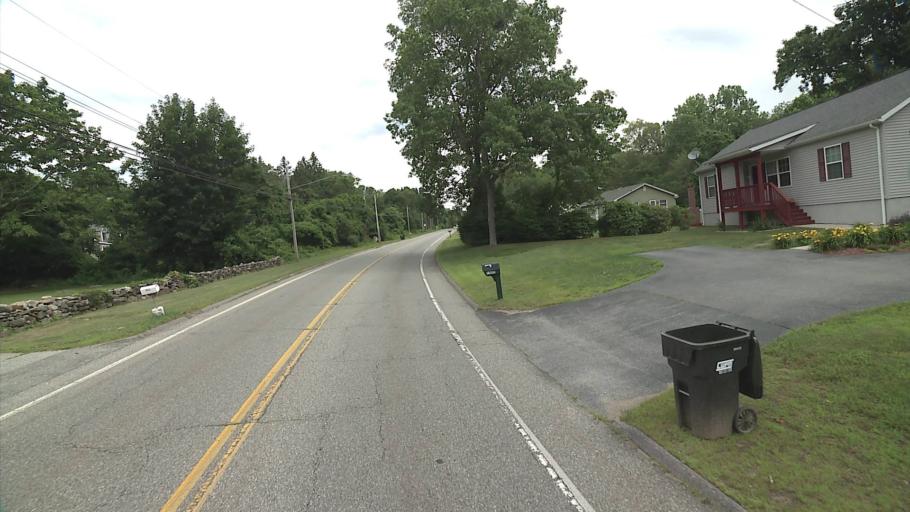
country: US
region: Connecticut
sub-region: New London County
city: Conning Towers-Nautilus Park
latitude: 41.3945
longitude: -72.0274
